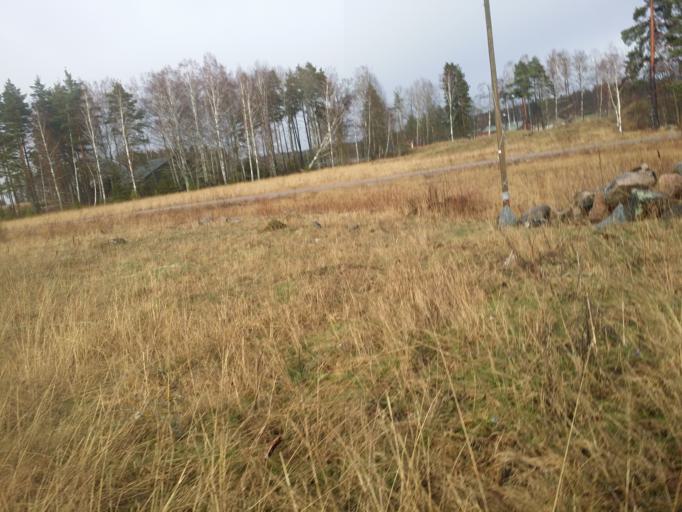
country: SE
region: Soedermanland
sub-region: Eskilstuna Kommun
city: Arla
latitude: 59.3423
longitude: 16.6994
